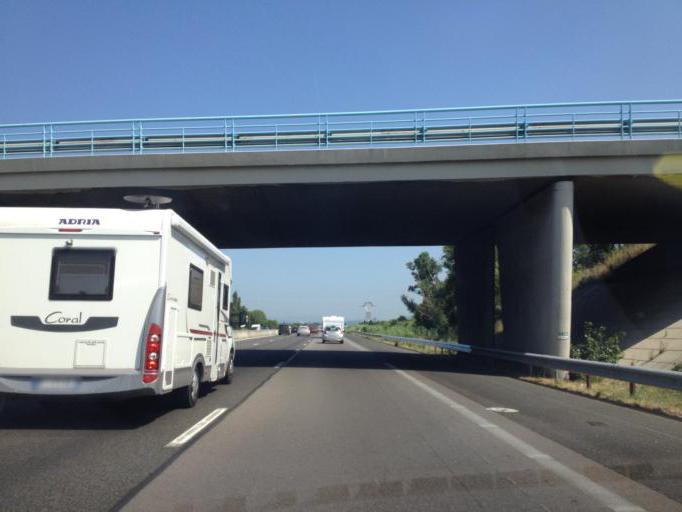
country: FR
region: Rhone-Alpes
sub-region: Departement de la Drome
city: Saint-Paul-Trois-Chateaux
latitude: 44.3650
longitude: 4.7355
